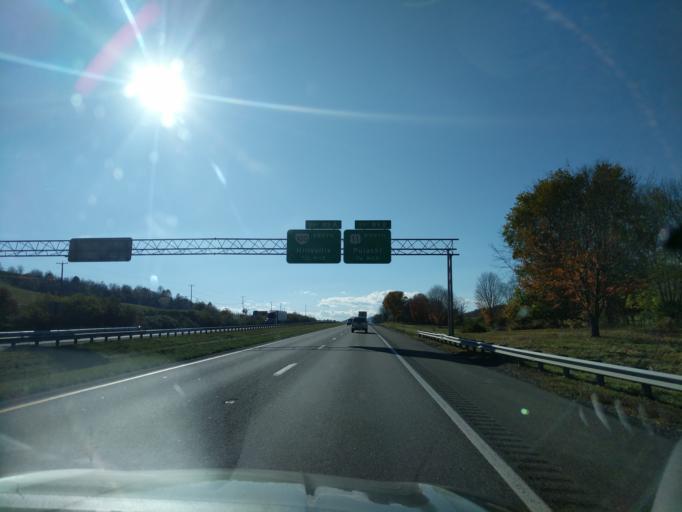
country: US
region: Virginia
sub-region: Pulaski County
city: Pulaski
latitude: 36.9982
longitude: -80.7793
